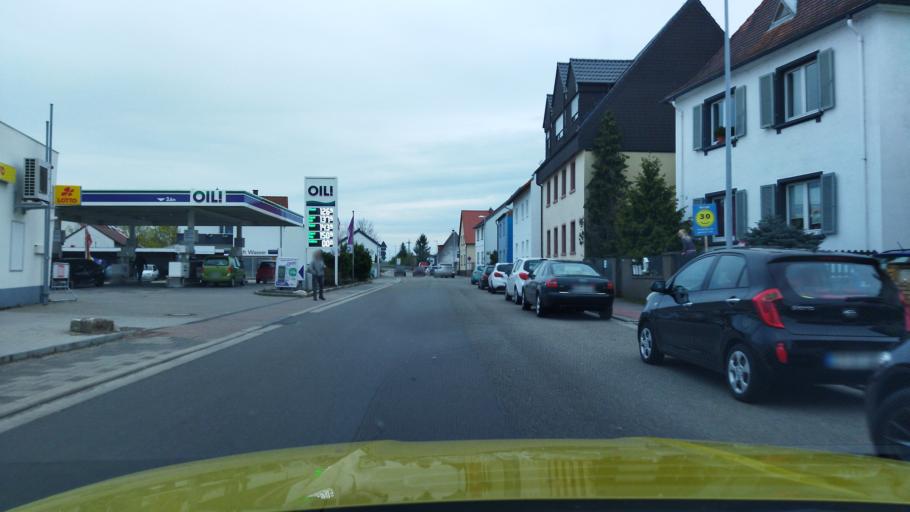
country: DE
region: Rheinland-Pfalz
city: Dudenhofen
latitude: 49.3160
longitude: 8.3963
